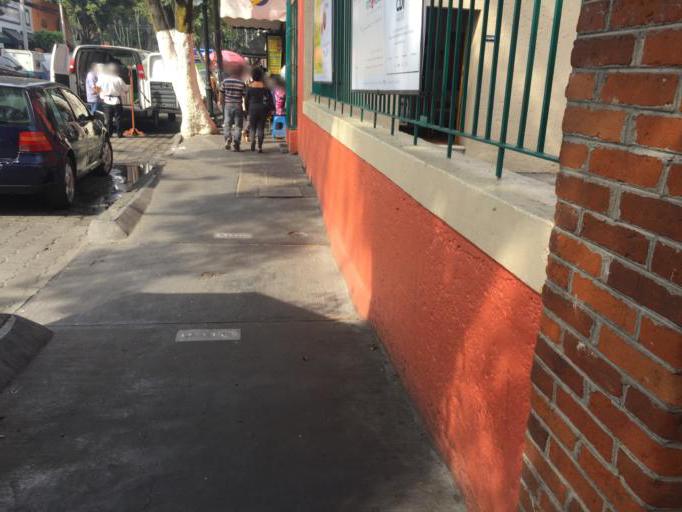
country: MX
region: Mexico City
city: Coyoacan
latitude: 19.3497
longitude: -99.1610
